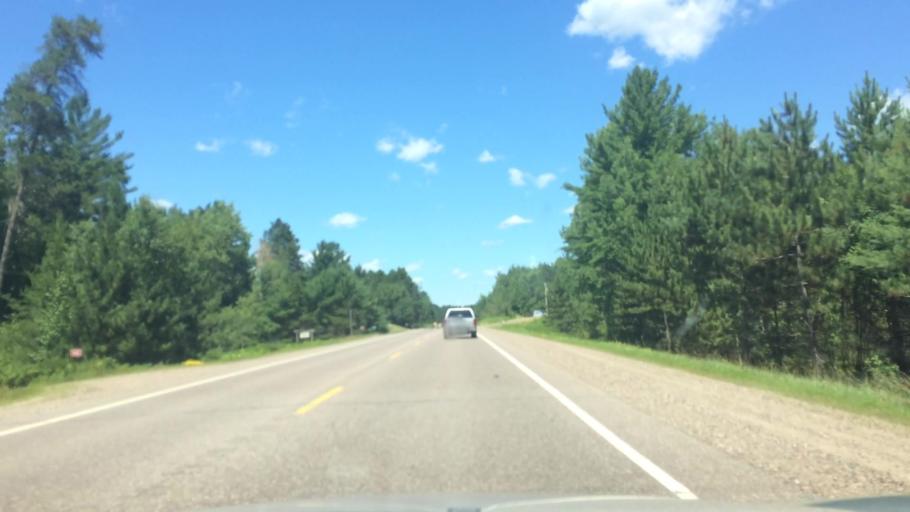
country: US
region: Wisconsin
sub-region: Lincoln County
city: Tomahawk
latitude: 45.6470
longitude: -89.7049
